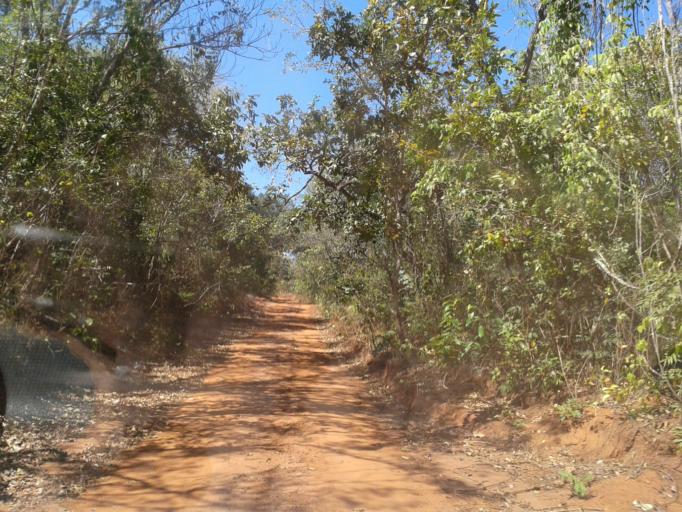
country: BR
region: Minas Gerais
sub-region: Monte Alegre De Minas
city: Monte Alegre de Minas
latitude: -18.8303
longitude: -49.1032
